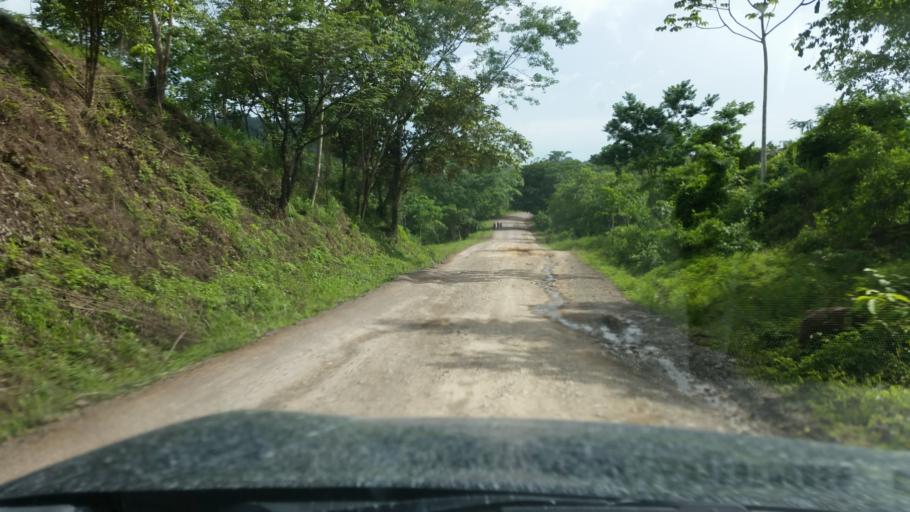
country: NI
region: Atlantico Norte (RAAN)
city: Siuna
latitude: 13.5958
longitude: -84.8053
